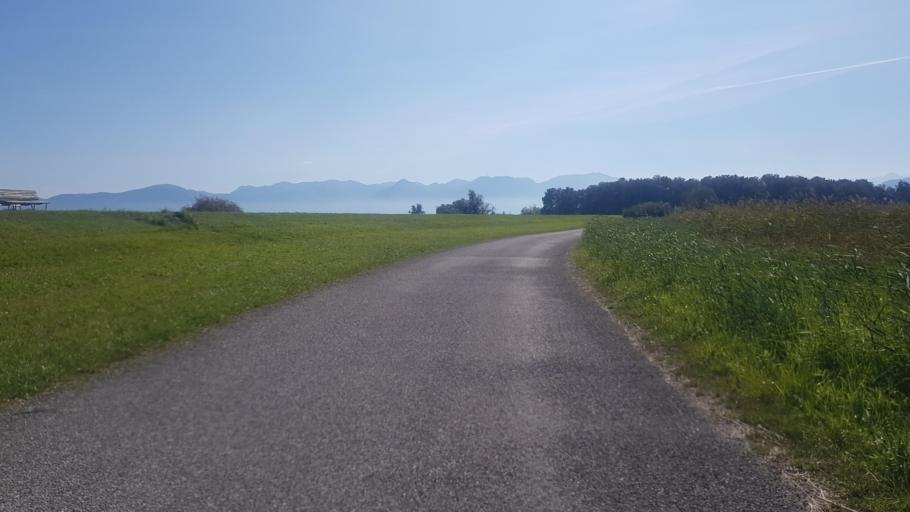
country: AT
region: Vorarlberg
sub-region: Politischer Bezirk Bregenz
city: Fussach
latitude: 47.4972
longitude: 9.6367
